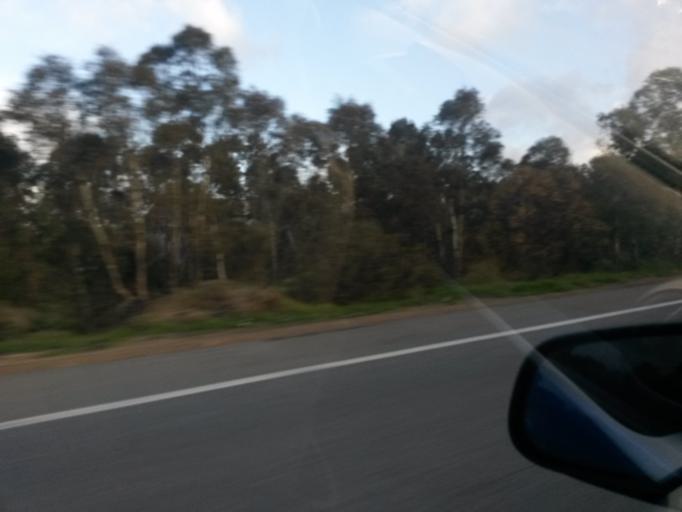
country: AU
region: South Australia
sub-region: Port Adelaide Enfield
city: Alberton
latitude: -34.8353
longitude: 138.5295
